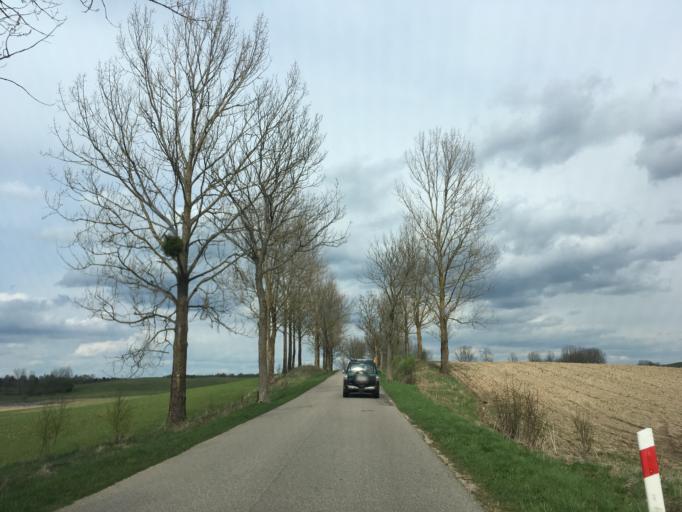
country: PL
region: Podlasie
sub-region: Powiat suwalski
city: Filipow
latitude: 54.3556
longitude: 22.7613
